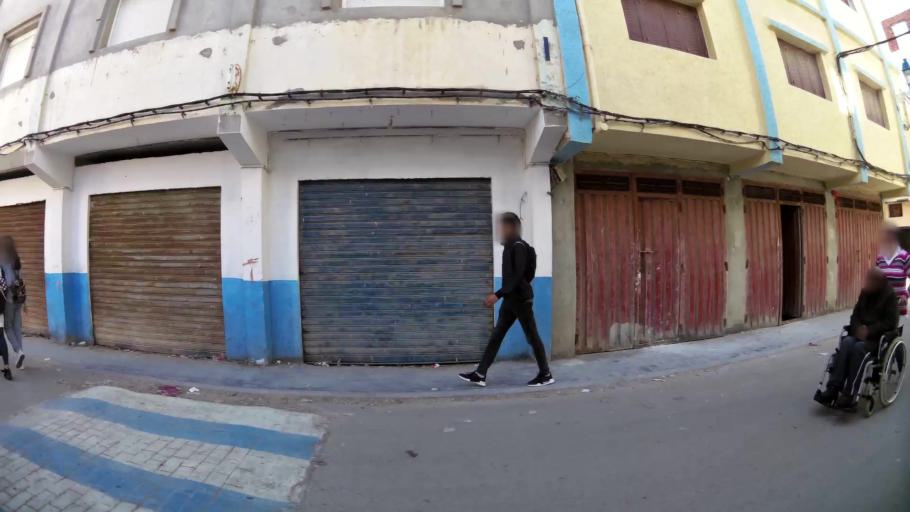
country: MA
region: Tanger-Tetouan
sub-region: Tetouan
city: Martil
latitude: 35.6112
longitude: -5.2728
